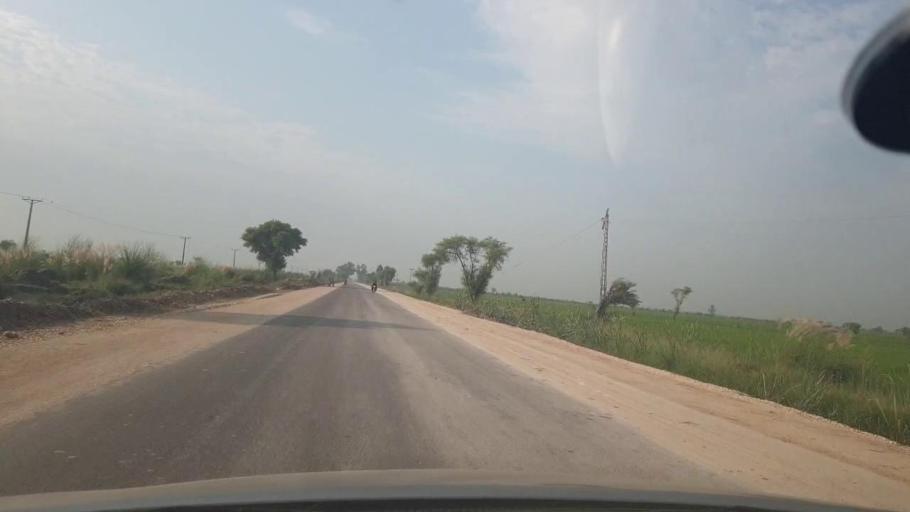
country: PK
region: Sindh
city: Jacobabad
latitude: 28.1903
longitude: 68.3675
